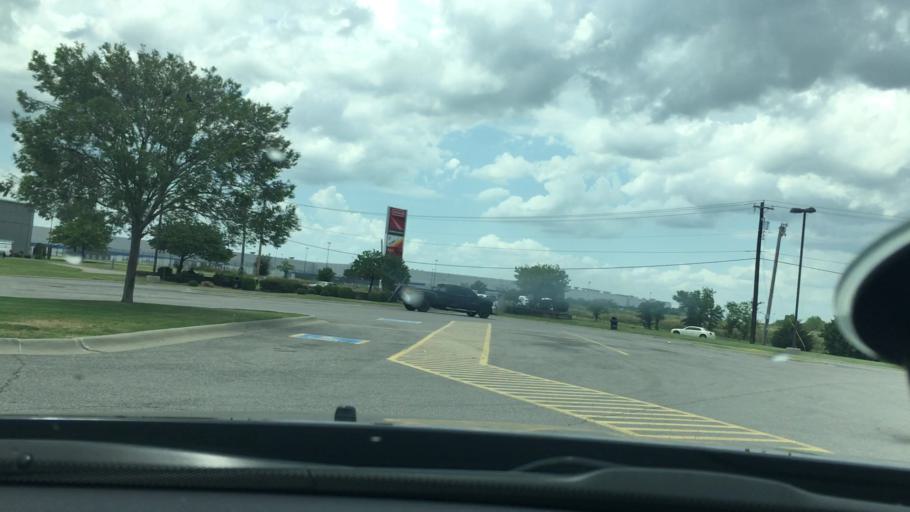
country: US
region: Oklahoma
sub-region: Carter County
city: Ardmore
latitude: 34.2011
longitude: -97.1677
